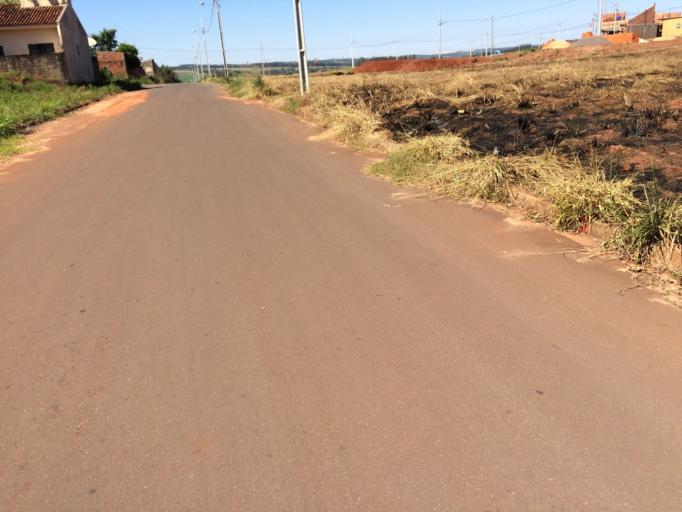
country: BR
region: Parana
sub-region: Cianorte
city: Cianorte
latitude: -23.5387
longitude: -52.5946
